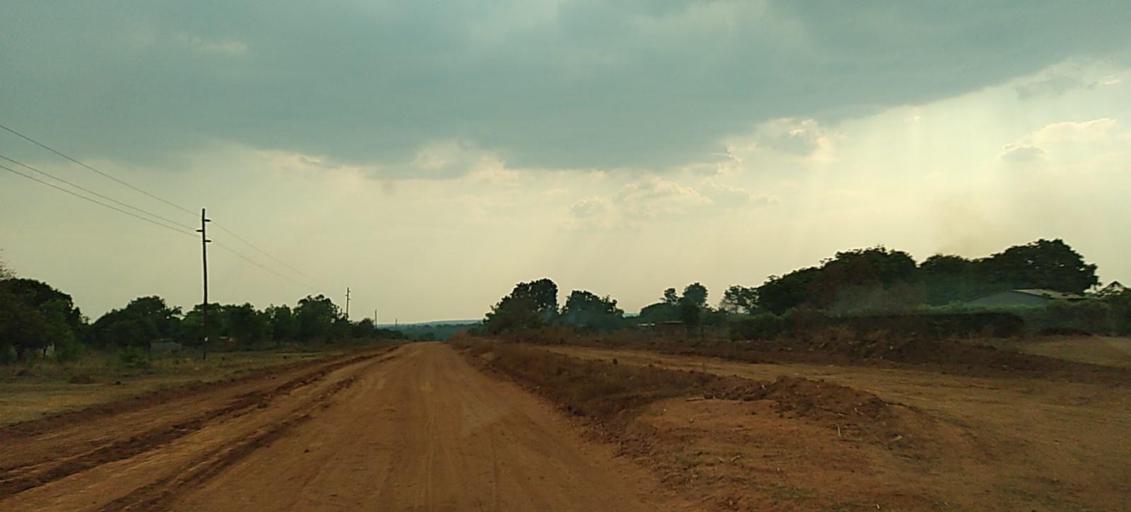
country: ZM
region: Copperbelt
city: Kalulushi
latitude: -12.9334
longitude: 27.9360
